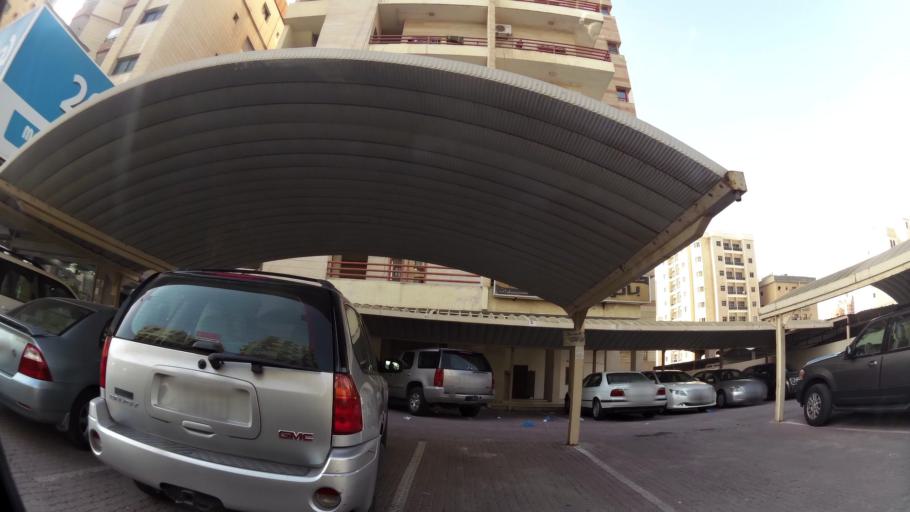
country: KW
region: Muhafazat Hawalli
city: As Salimiyah
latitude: 29.3347
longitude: 48.0843
